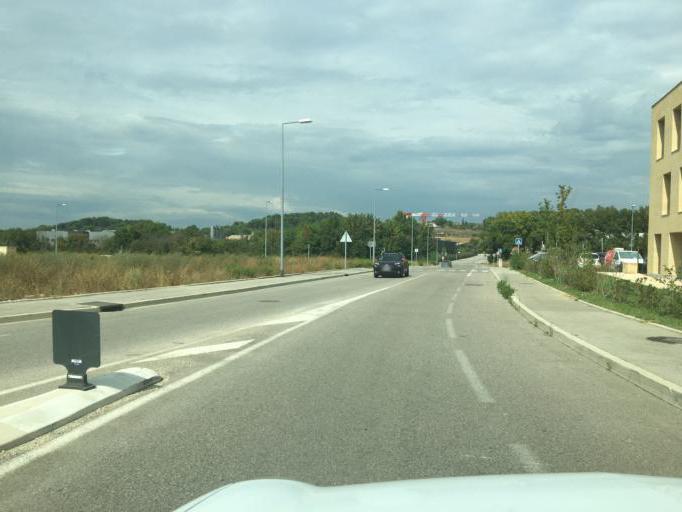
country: FR
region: Provence-Alpes-Cote d'Azur
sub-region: Departement des Bouches-du-Rhone
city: Bouc-Bel-Air
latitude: 43.4795
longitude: 5.3940
